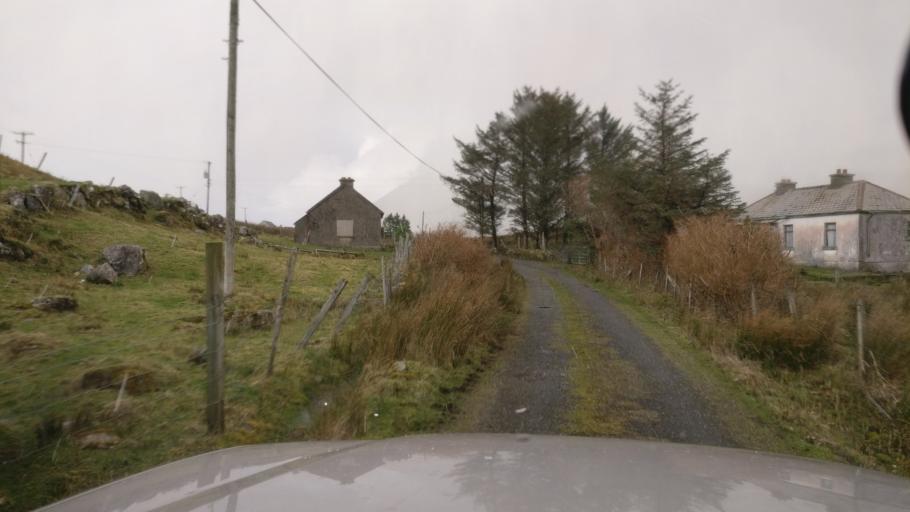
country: IE
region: Connaught
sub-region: County Galway
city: Clifden
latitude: 53.4887
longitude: -9.6984
